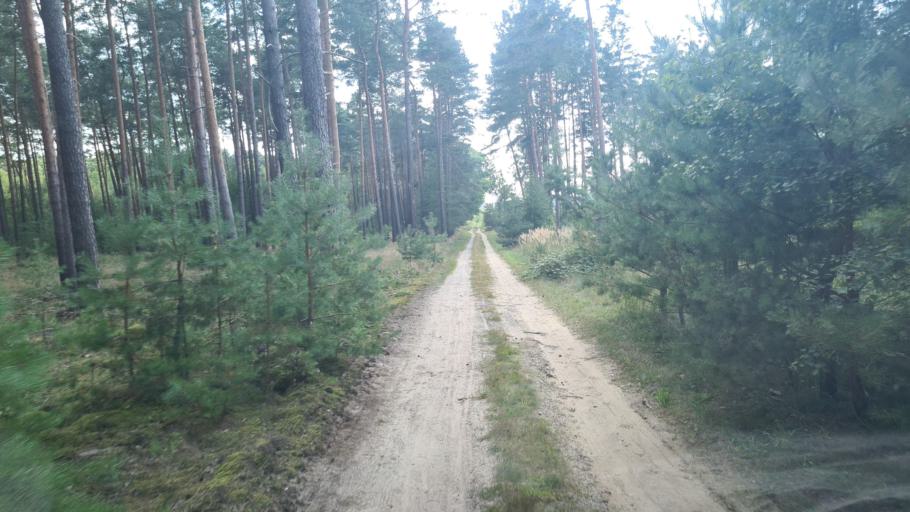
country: DE
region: Brandenburg
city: Schonewalde
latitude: 51.7432
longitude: 13.5962
